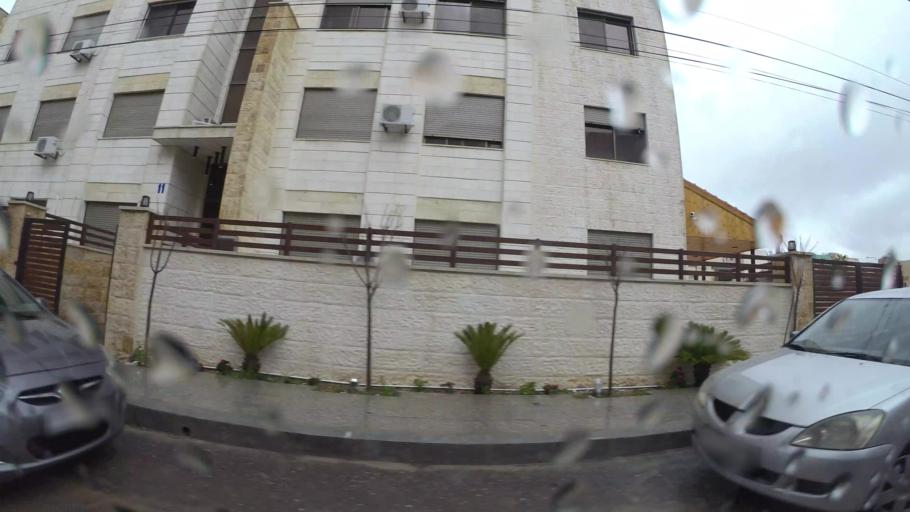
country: JO
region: Amman
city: Al Jubayhah
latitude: 32.0237
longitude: 35.8721
